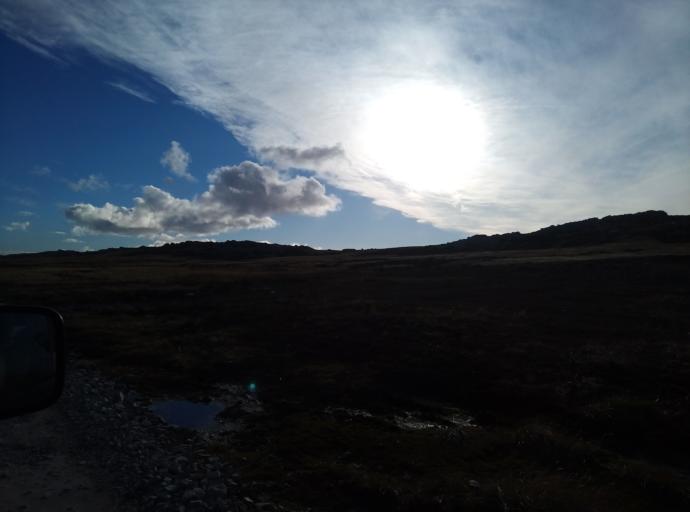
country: FK
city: Stanley
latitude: -51.6843
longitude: -57.9006
